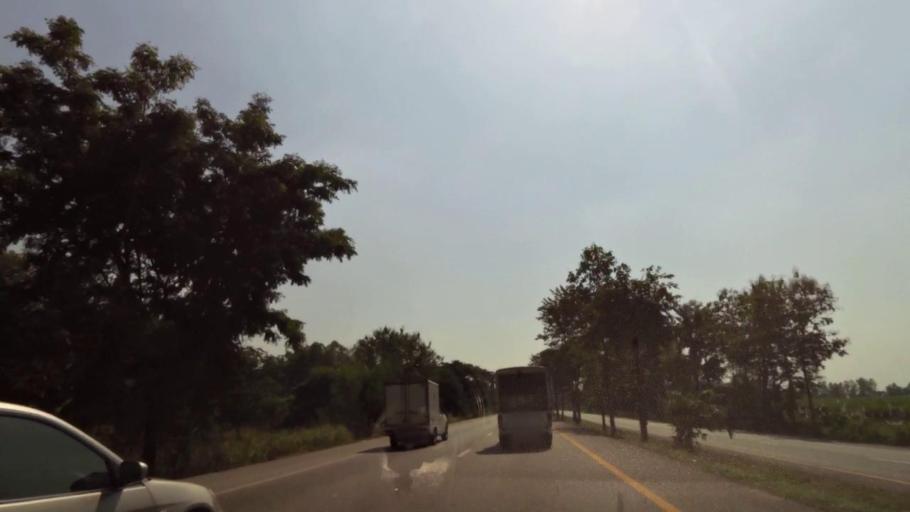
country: TH
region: Phichit
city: Bueng Na Rang
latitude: 16.1082
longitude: 100.1258
